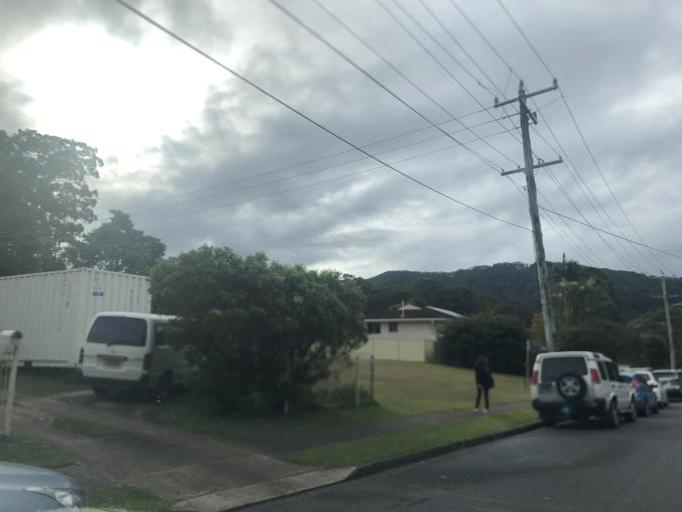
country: AU
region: New South Wales
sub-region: Coffs Harbour
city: Coffs Harbour
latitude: -30.2830
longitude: 153.1116
